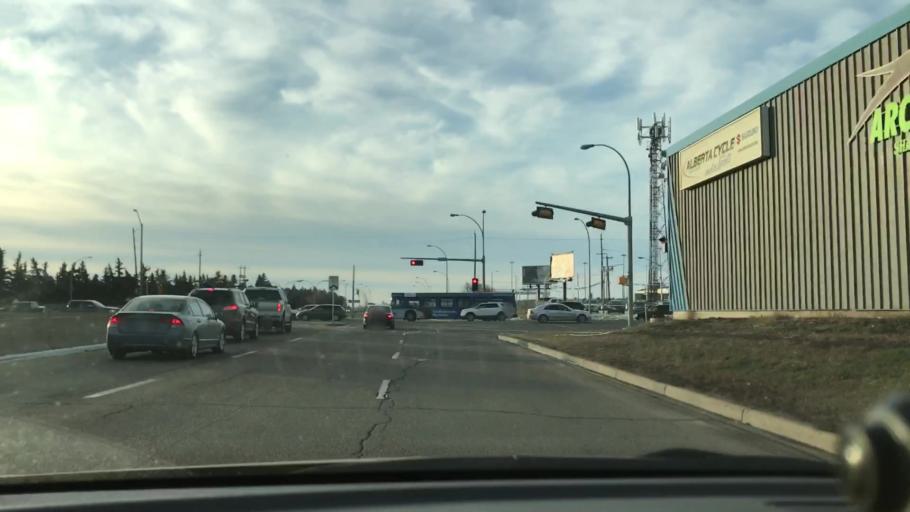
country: CA
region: Alberta
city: Edmonton
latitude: 53.5816
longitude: -113.4910
